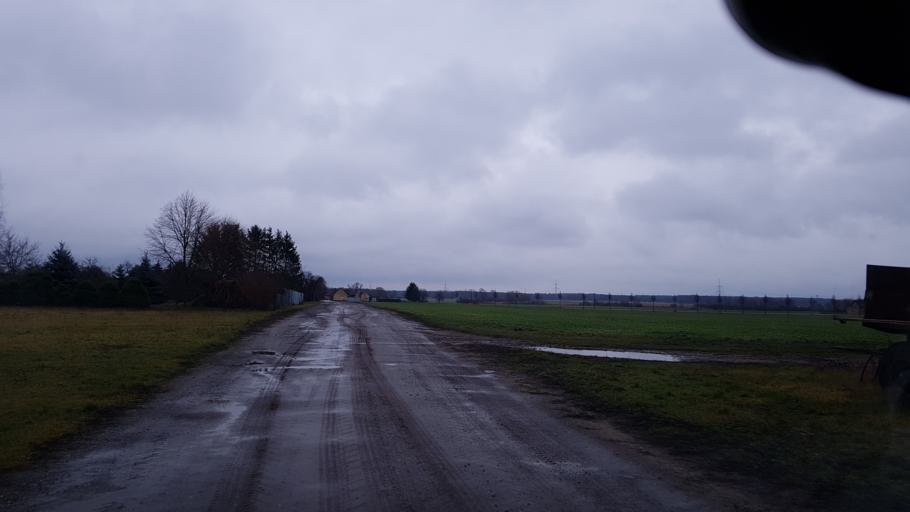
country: DE
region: Brandenburg
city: Sallgast
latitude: 51.6402
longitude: 13.8522
